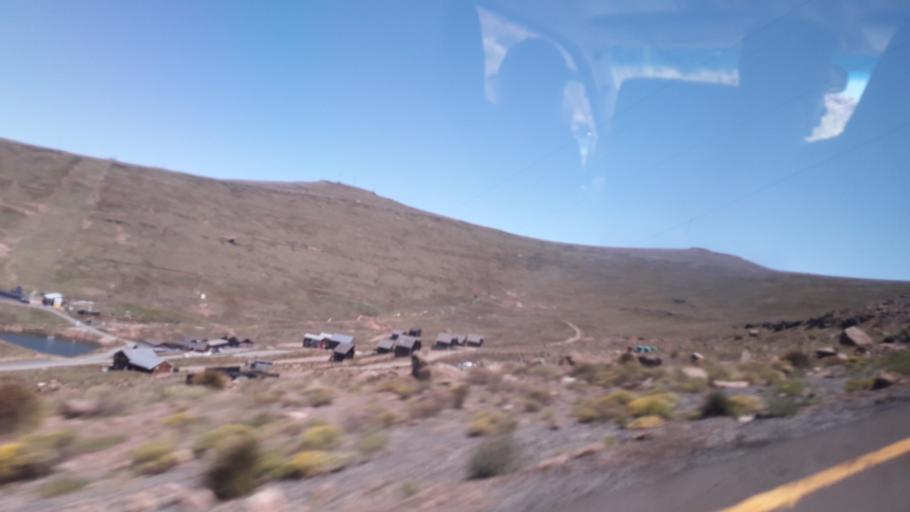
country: ZA
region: Orange Free State
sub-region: Thabo Mofutsanyana District Municipality
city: Phuthaditjhaba
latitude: -28.8261
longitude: 28.7309
